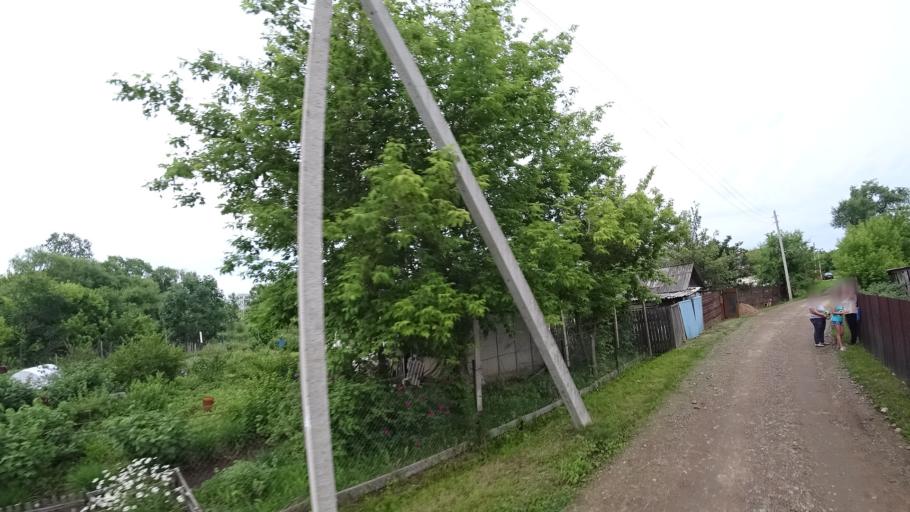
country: RU
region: Primorskiy
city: Novosysoyevka
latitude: 44.2274
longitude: 133.3538
